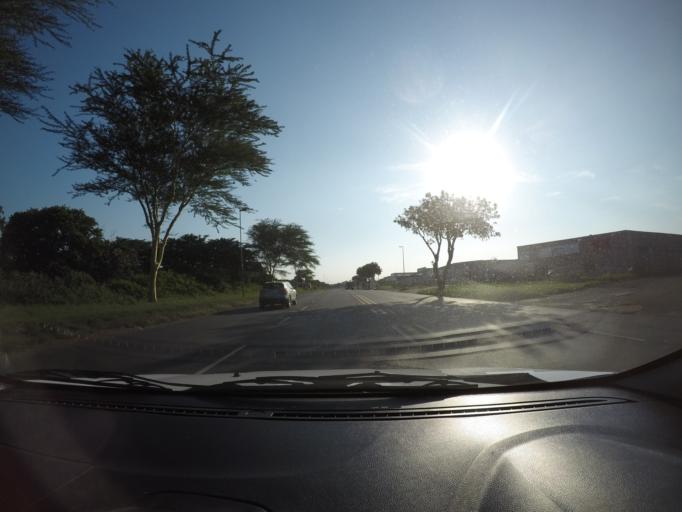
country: ZA
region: KwaZulu-Natal
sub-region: uThungulu District Municipality
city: Richards Bay
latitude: -28.7660
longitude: 32.0177
